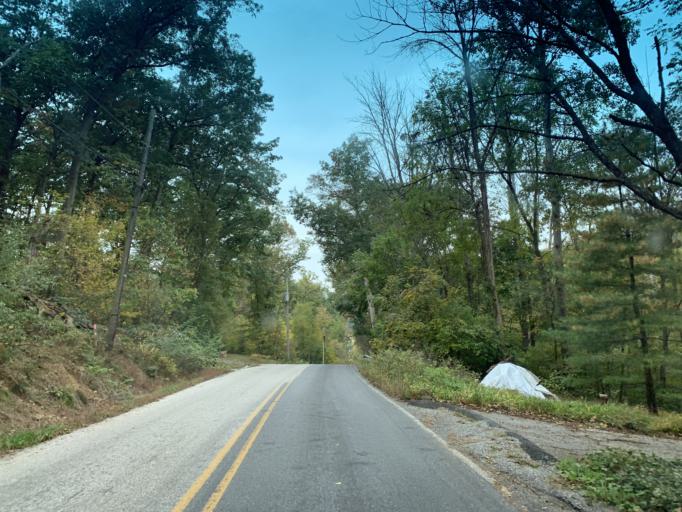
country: US
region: Pennsylvania
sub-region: York County
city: Susquehanna Trails
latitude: 39.8159
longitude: -76.4739
